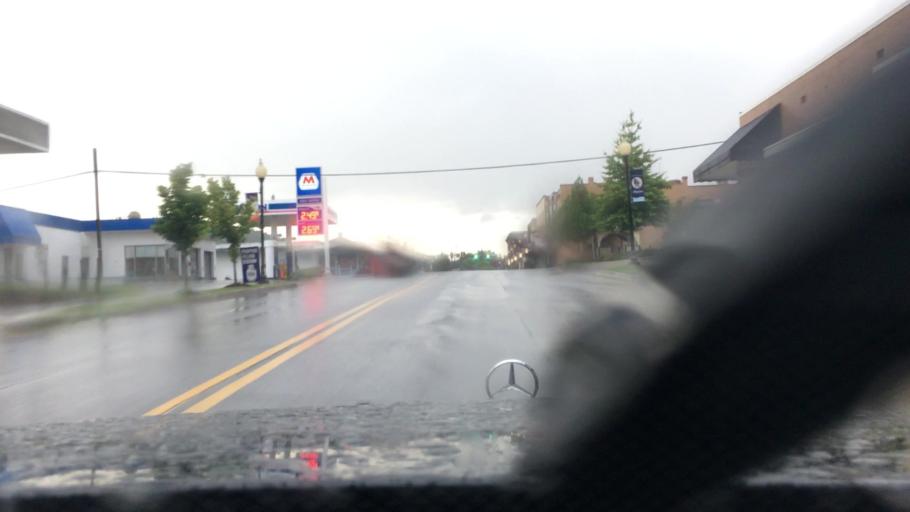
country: US
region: Virginia
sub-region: Campbell County
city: Altavista
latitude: 37.1100
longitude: -79.2882
